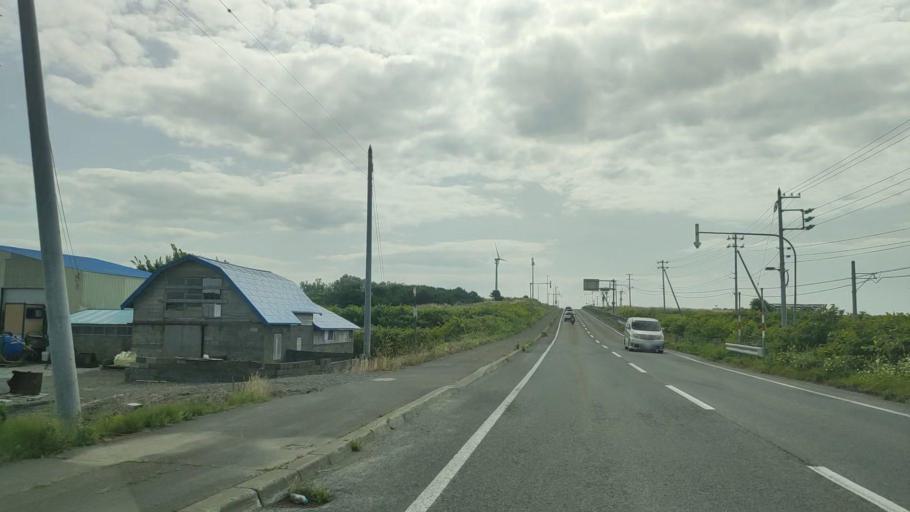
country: JP
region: Hokkaido
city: Rumoi
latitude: 44.4101
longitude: 141.7330
